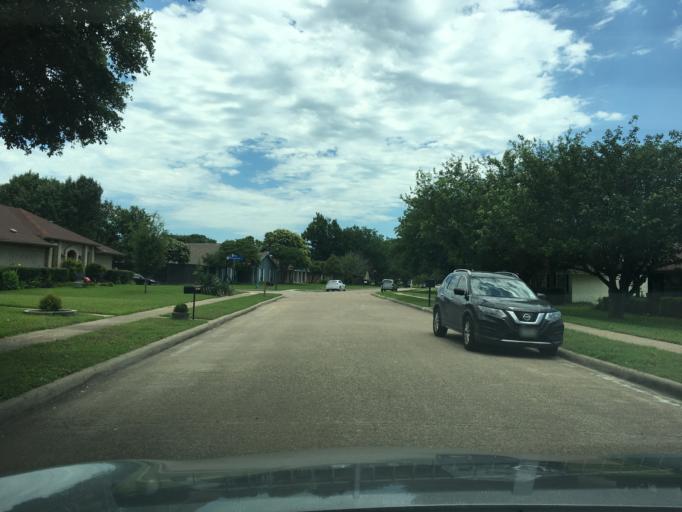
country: US
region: Texas
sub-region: Dallas County
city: Richardson
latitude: 32.9345
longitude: -96.6861
